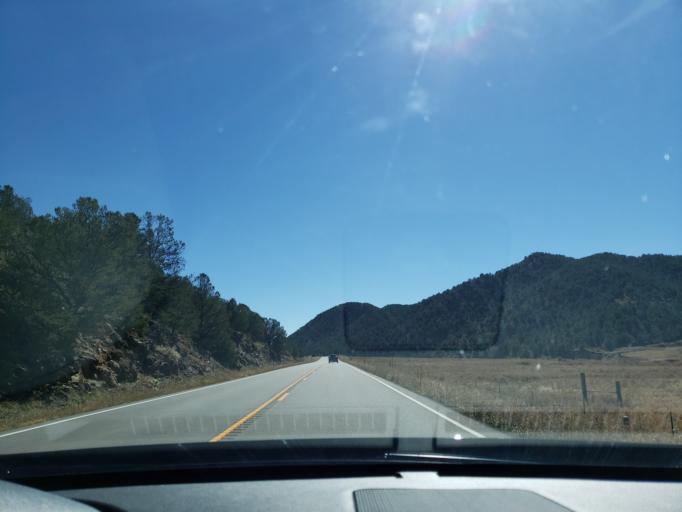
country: US
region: Colorado
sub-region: Fremont County
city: Canon City
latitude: 38.6265
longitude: -105.4580
